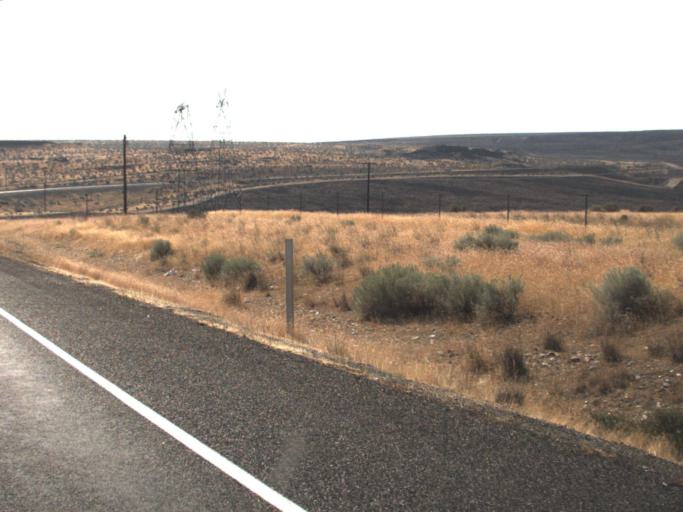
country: US
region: Washington
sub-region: Grant County
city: Desert Aire
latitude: 46.6167
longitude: -119.7266
